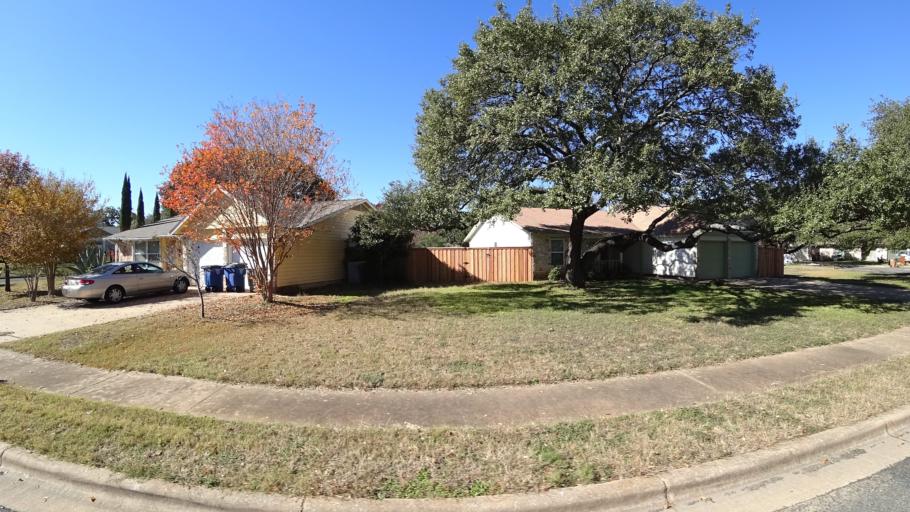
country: US
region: Texas
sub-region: Travis County
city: Wells Branch
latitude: 30.4200
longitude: -97.7148
